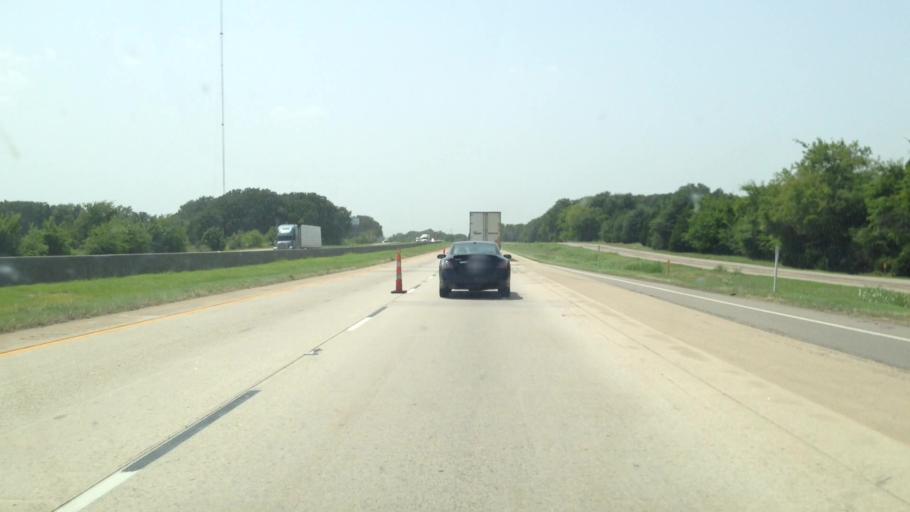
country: US
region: Texas
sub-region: Hopkins County
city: Sulphur Springs
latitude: 33.1245
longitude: -95.7368
